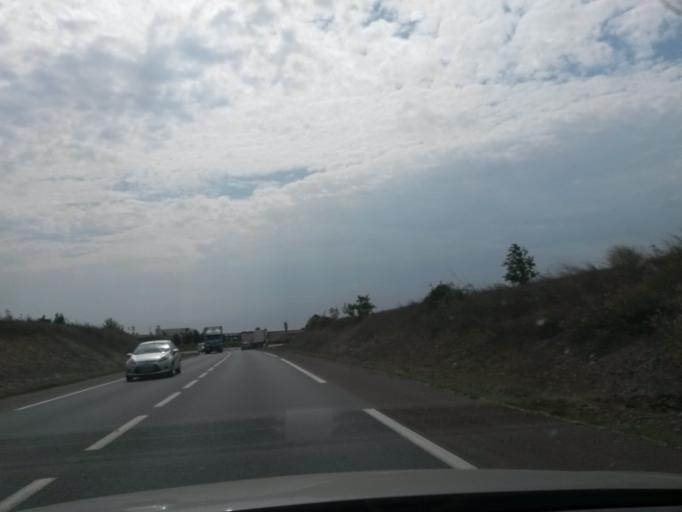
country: FR
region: Poitou-Charentes
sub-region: Departement de la Charente-Maritime
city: Saint-Xandre
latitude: 46.1829
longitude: -1.0922
